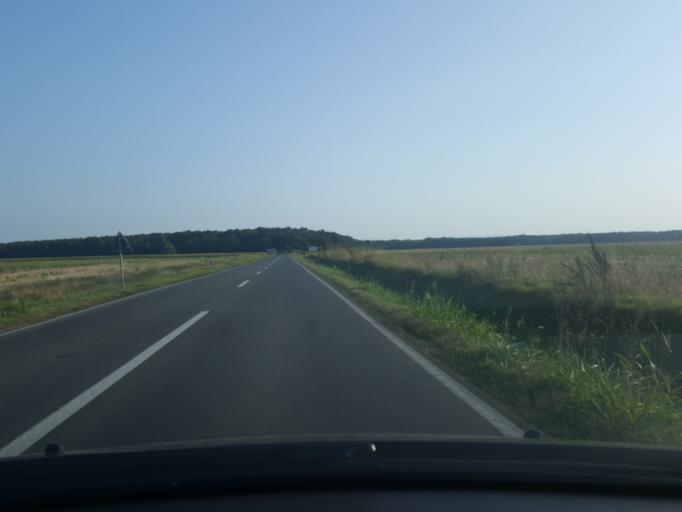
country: RS
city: Hrtkovci
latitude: 44.8479
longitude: 19.7689
